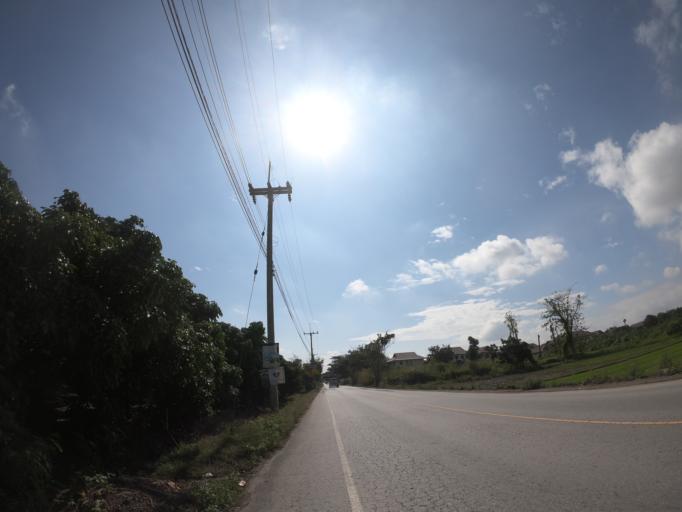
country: TH
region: Chiang Mai
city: Hang Dong
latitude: 18.6993
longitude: 98.9645
